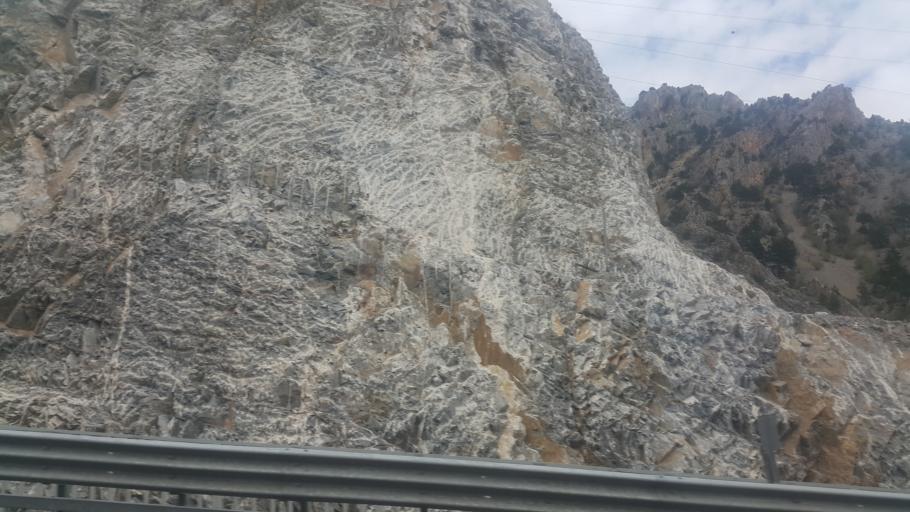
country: TR
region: Adana
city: Pozanti
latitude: 37.4744
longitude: 34.8609
